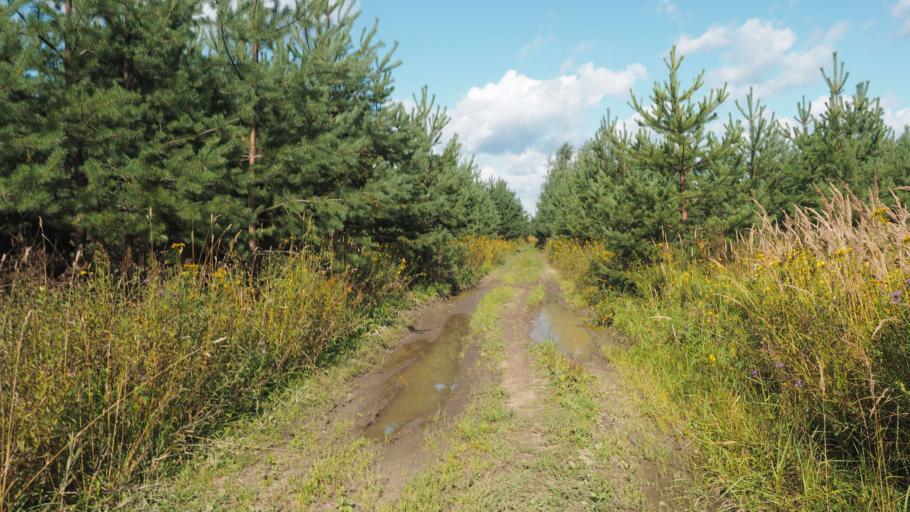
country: RU
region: Moskovskaya
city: Ramenskoye
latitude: 55.5956
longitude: 38.2870
